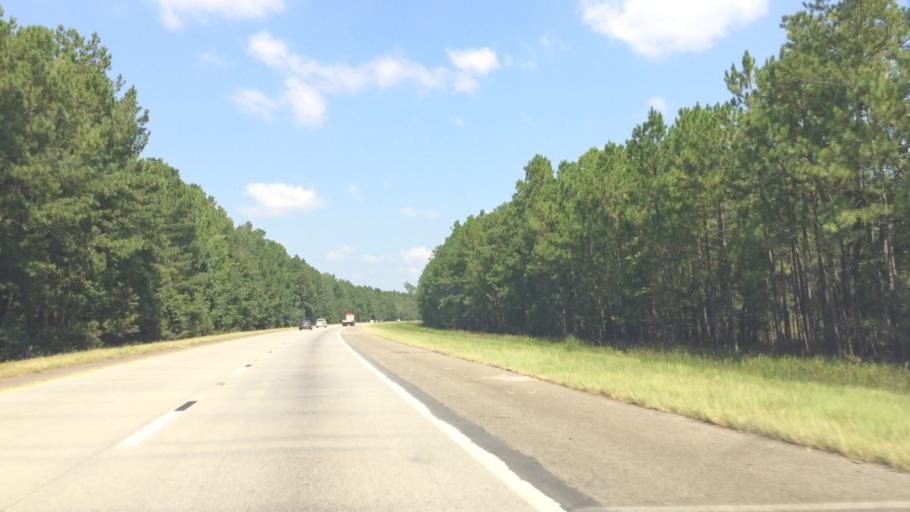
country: US
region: South Carolina
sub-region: Colleton County
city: Walterboro
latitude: 33.0427
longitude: -80.6692
